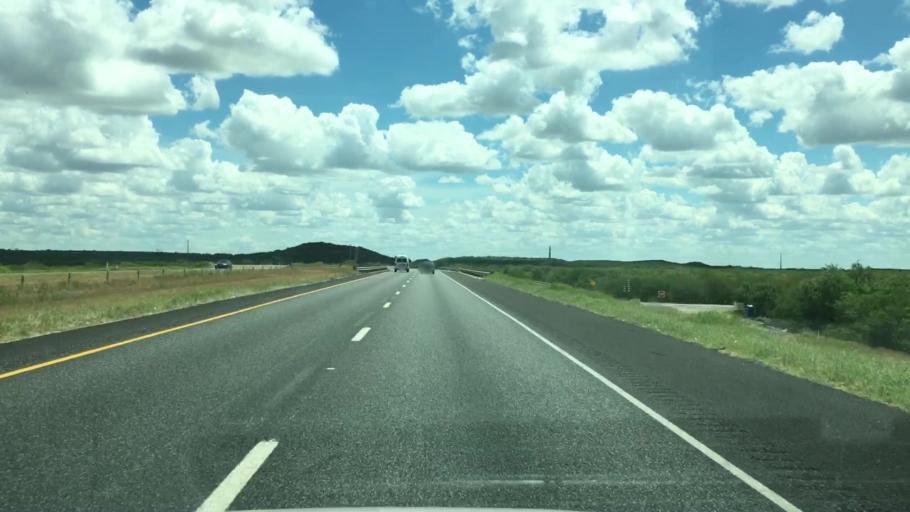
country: US
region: Texas
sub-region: Live Oak County
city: Three Rivers
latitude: 28.7352
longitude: -98.2899
